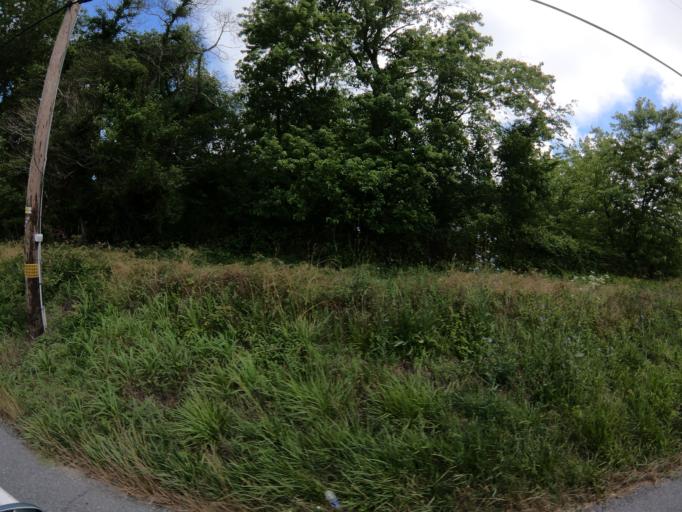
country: US
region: Maryland
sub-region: Caroline County
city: Greensboro
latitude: 39.0351
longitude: -75.7761
